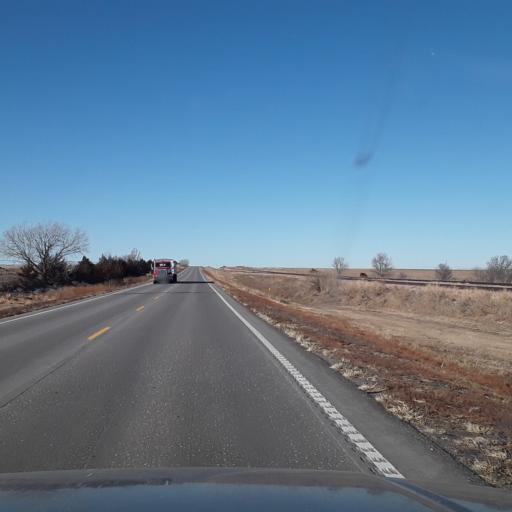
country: US
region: Nebraska
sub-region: Phelps County
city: Holdrege
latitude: 40.4815
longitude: -99.5137
